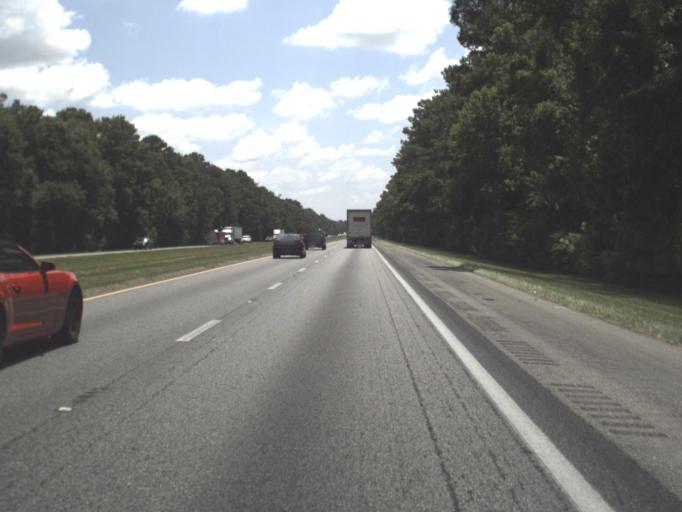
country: US
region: Florida
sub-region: Jefferson County
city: Monticello
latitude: 30.4447
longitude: -83.6944
